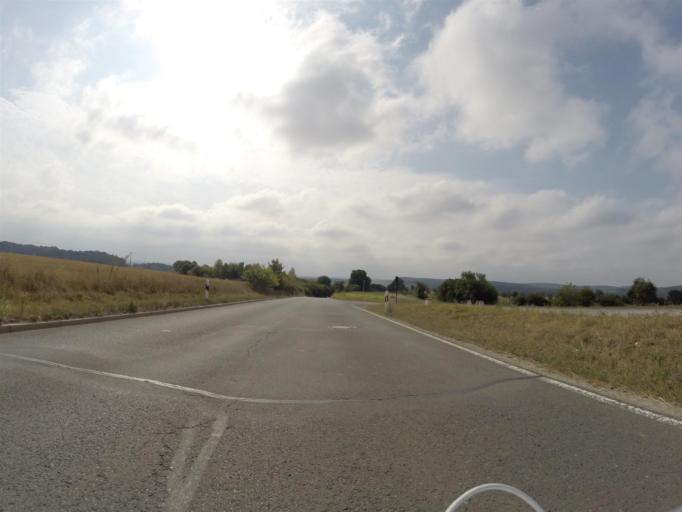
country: DE
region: Thuringia
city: Rausdorf
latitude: 50.8783
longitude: 11.6949
